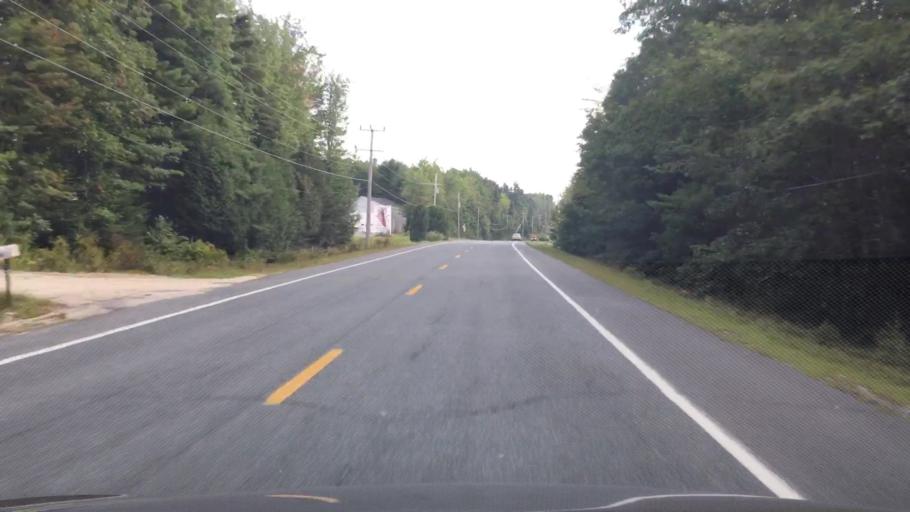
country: US
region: Maine
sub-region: Hancock County
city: Surry
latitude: 44.4861
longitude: -68.5131
